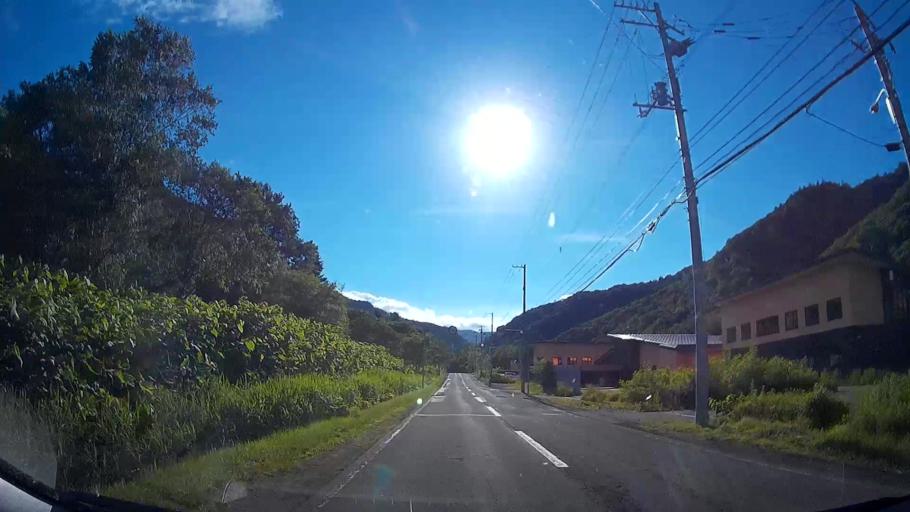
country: JP
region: Hokkaido
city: Sapporo
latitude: 42.9729
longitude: 141.1592
